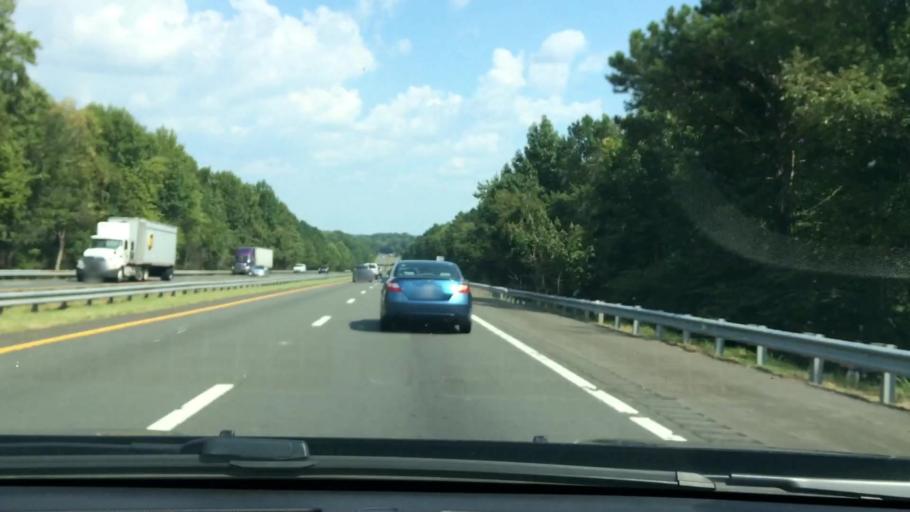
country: US
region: North Carolina
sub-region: Orange County
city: Hillsborough
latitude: 36.0440
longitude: -79.0393
